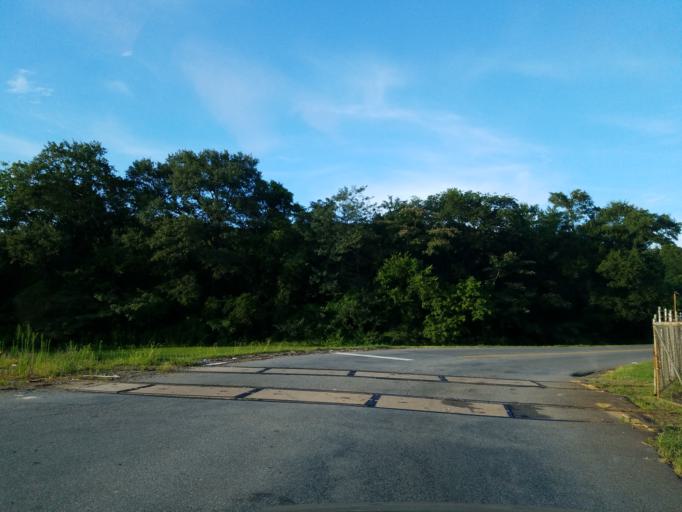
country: US
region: Georgia
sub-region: Bartow County
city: Cartersville
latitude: 34.1523
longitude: -84.7875
